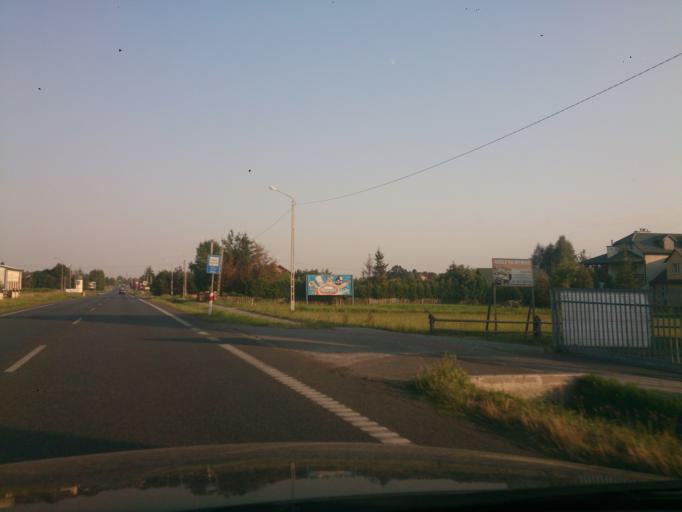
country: PL
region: Subcarpathian Voivodeship
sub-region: Powiat kolbuszowski
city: Kolbuszowa
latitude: 50.2610
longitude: 21.7620
